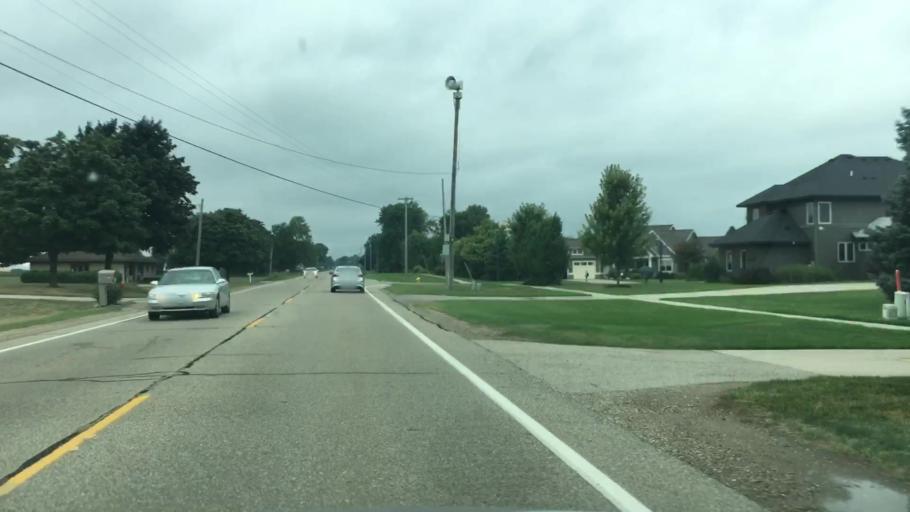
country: US
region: Michigan
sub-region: Ottawa County
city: Hudsonville
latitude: 42.8708
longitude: -85.8255
